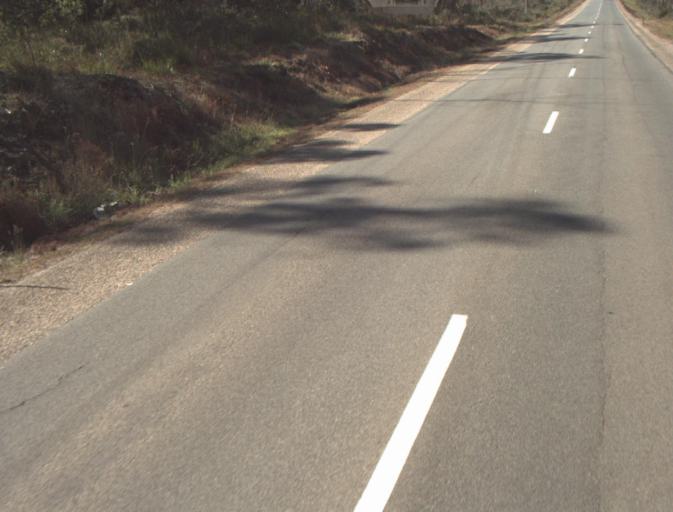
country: AU
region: Tasmania
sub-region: Launceston
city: Mayfield
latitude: -41.3169
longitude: 147.1929
